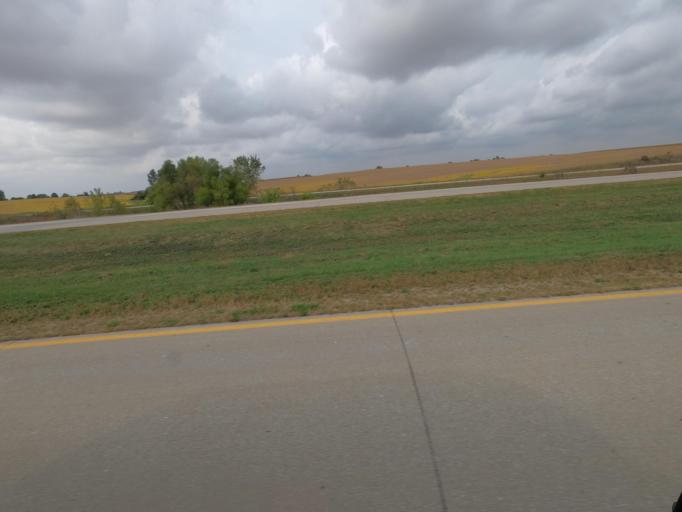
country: US
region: Iowa
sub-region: Wapello County
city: Ottumwa
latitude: 41.0041
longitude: -92.2975
